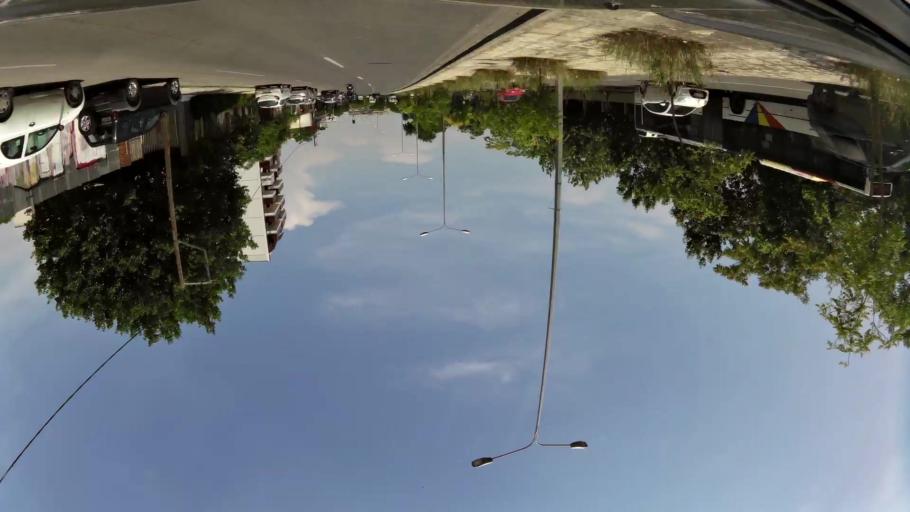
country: GR
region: Central Macedonia
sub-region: Nomos Thessalonikis
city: Thessaloniki
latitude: 40.6421
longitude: 22.9245
